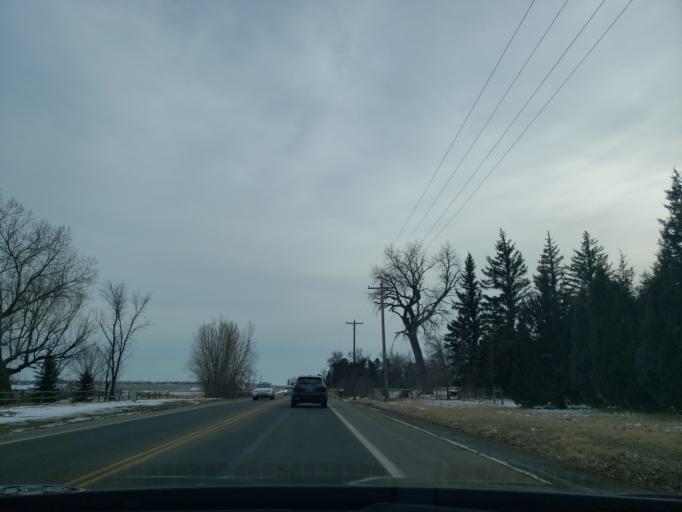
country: US
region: Colorado
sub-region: Larimer County
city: Fort Collins
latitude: 40.5062
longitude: -105.0963
